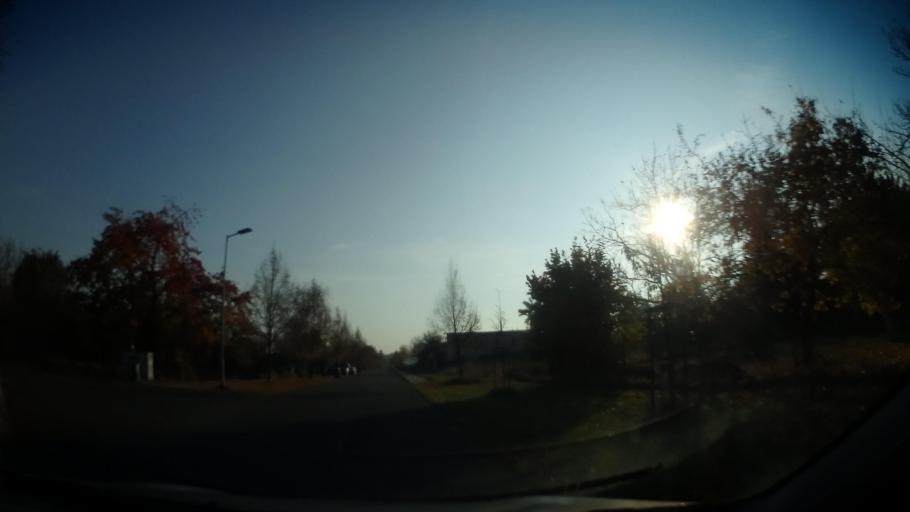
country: CZ
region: Central Bohemia
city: Sestajovice
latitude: 50.1014
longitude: 14.6808
